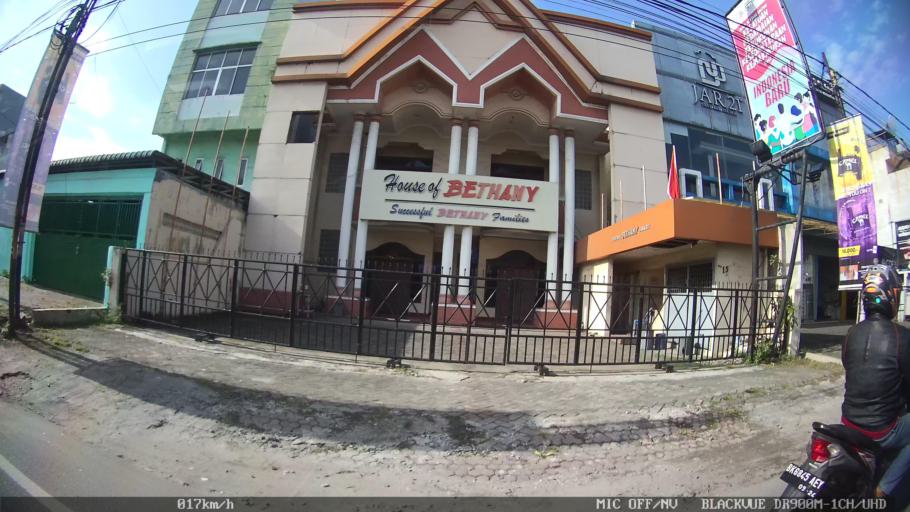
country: ID
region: North Sumatra
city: Medan
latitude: 3.6071
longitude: 98.6637
